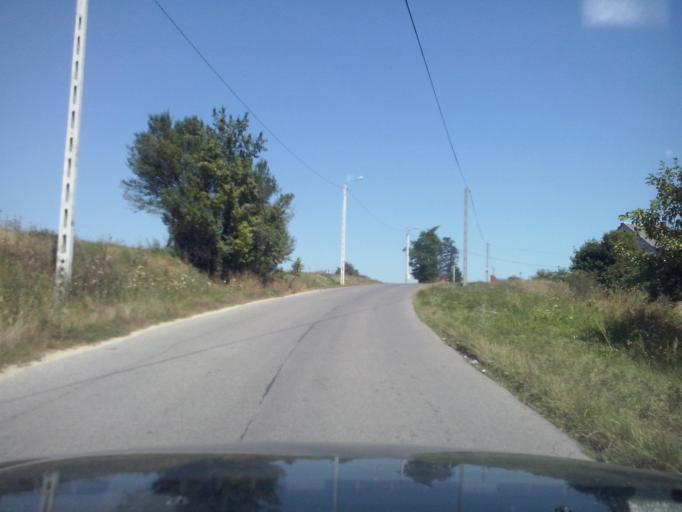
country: PL
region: Swietokrzyskie
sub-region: Powiat kielecki
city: Bieliny
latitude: 50.8072
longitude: 20.9570
